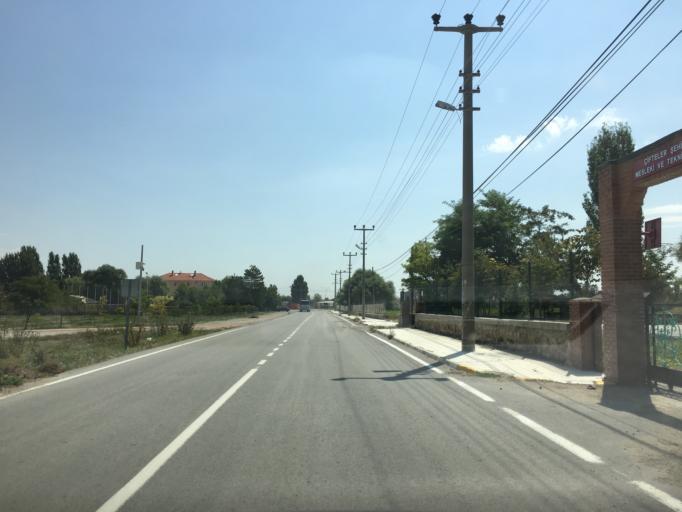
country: TR
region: Eskisehir
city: Cifteler
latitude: 39.3699
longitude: 31.0328
